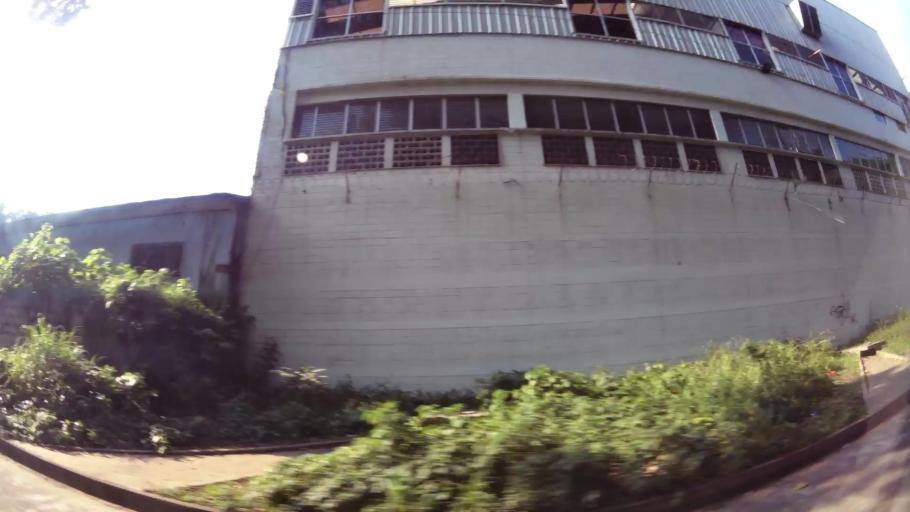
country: GT
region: Retalhuleu
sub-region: Municipio de Retalhuleu
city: Retalhuleu
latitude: 14.5298
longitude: -91.6843
